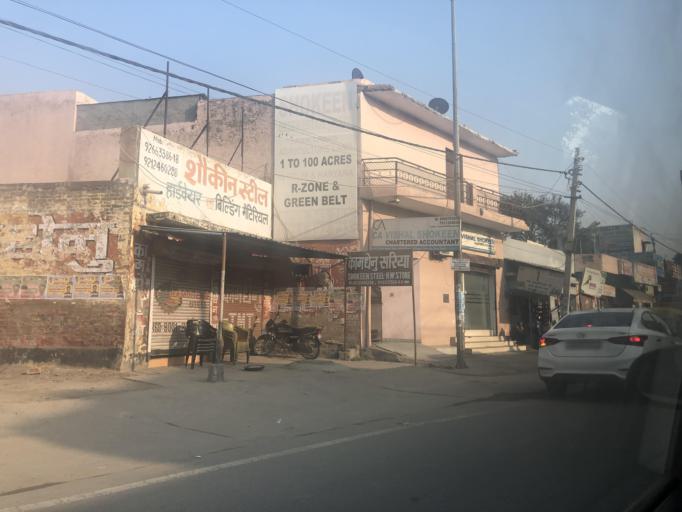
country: IN
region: Haryana
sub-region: Gurgaon
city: Gurgaon
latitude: 28.5585
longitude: 77.0040
